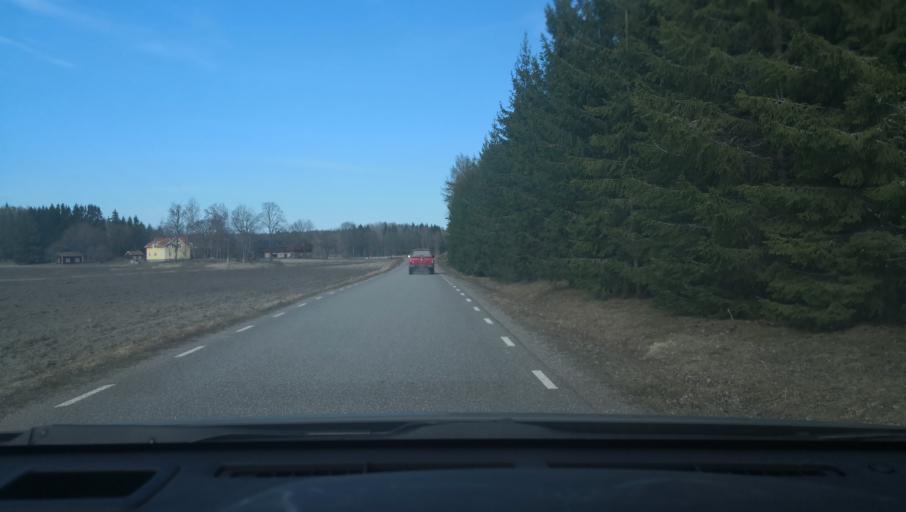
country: SE
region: Uppsala
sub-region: Heby Kommun
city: Heby
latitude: 59.8998
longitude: 16.8054
